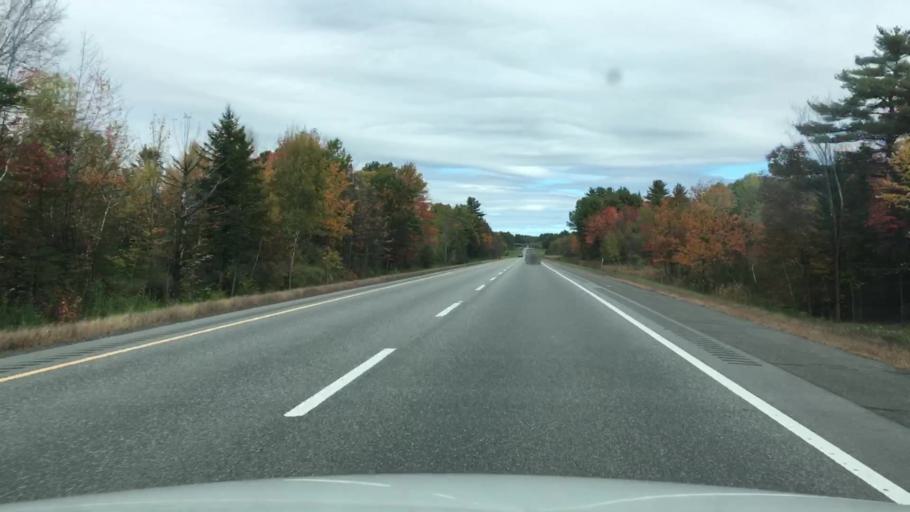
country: US
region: Maine
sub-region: Kennebec County
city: Sidney
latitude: 44.4422
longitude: -69.7245
